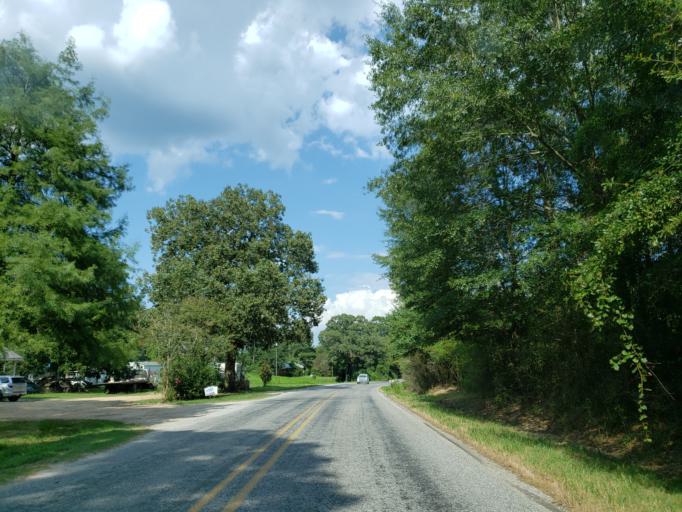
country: US
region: Mississippi
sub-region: Covington County
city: Collins
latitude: 31.6195
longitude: -89.3848
